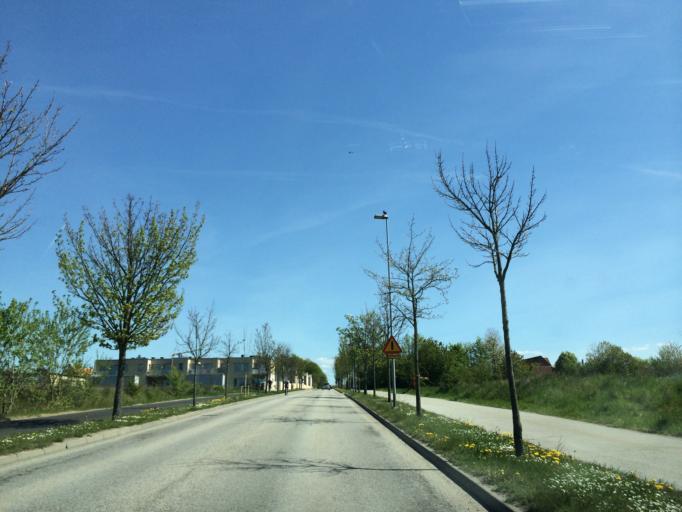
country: SE
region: Skane
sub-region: Staffanstorps Kommun
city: Hjaerup
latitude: 55.7037
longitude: 13.1506
